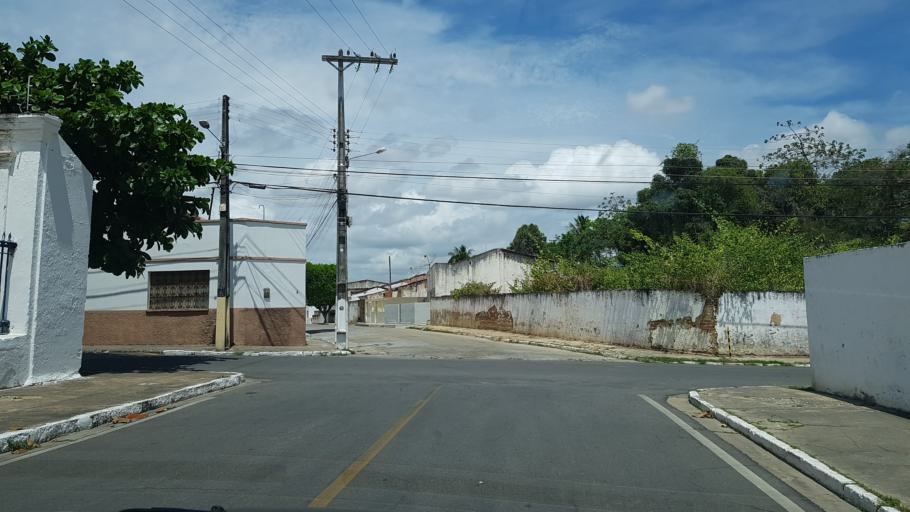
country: BR
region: Alagoas
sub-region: Penedo
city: Penedo
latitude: -10.2829
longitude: -36.5731
